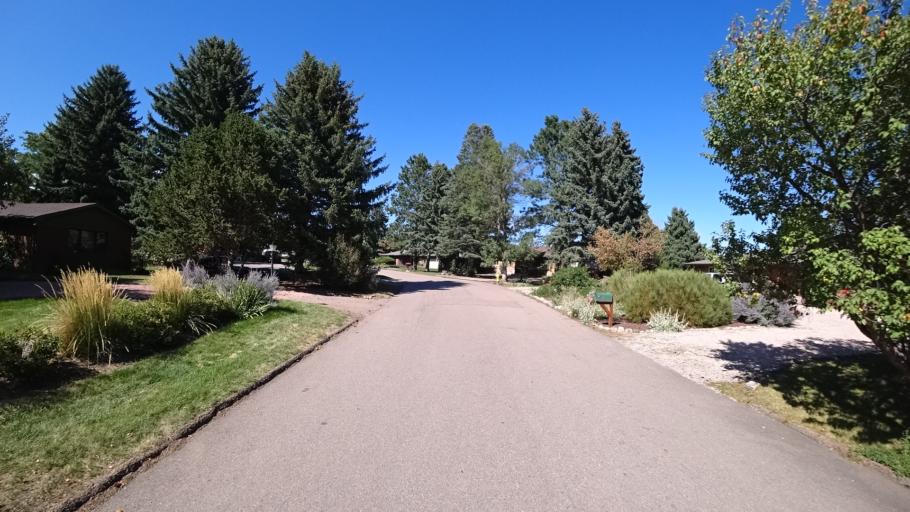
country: US
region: Colorado
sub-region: El Paso County
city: Colorado Springs
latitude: 38.8639
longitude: -104.8572
